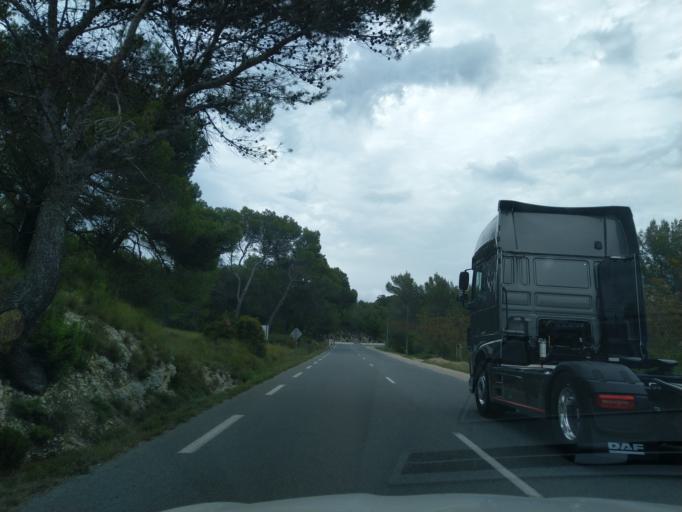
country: FR
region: Provence-Alpes-Cote d'Azur
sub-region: Departement des Bouches-du-Rhone
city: Cuges-les-Pins
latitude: 43.2656
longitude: 5.7460
